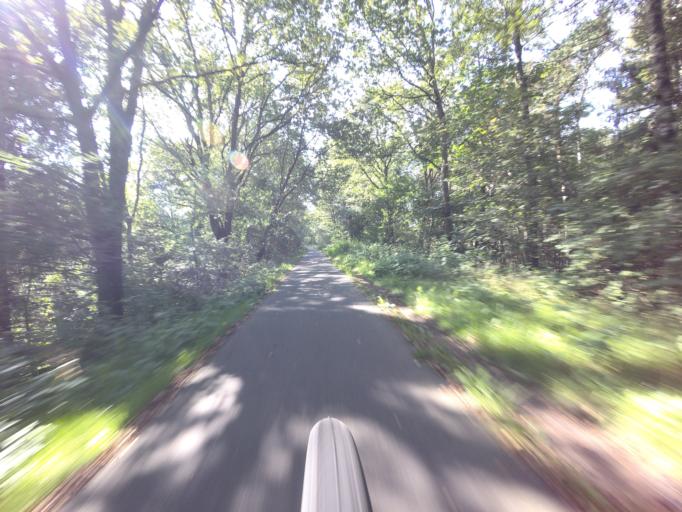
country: DK
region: Central Jutland
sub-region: Viborg Kommune
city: Viborg
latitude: 56.4131
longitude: 9.3643
